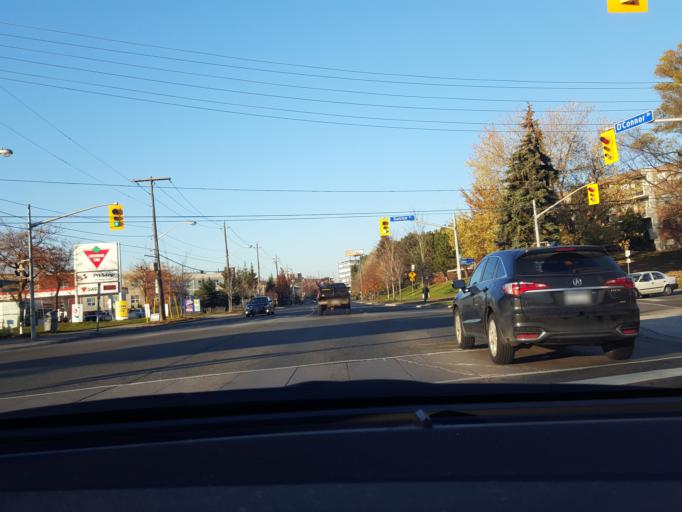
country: CA
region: Ontario
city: Scarborough
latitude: 43.7188
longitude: -79.3044
